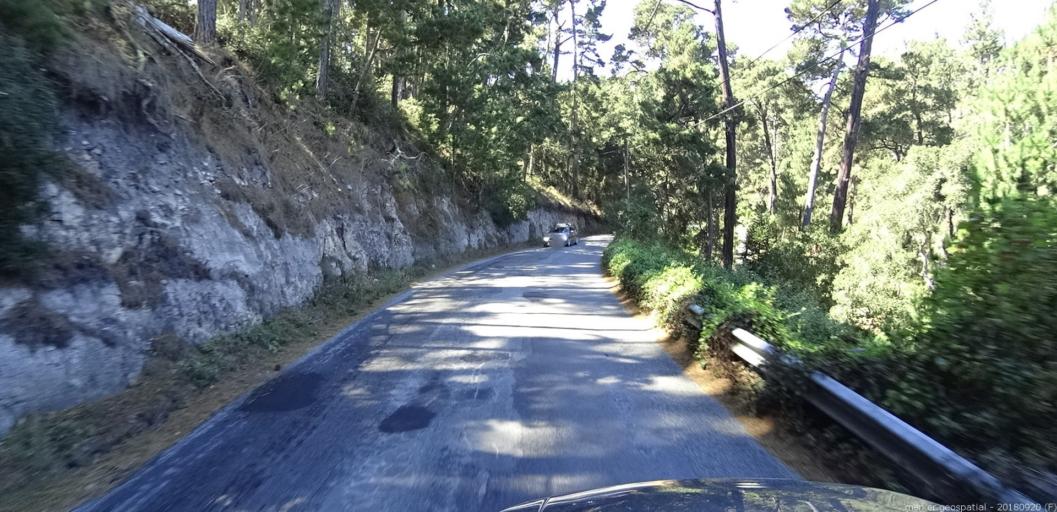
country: US
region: California
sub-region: Monterey County
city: Carmel-by-the-Sea
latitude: 36.5703
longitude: -121.9023
